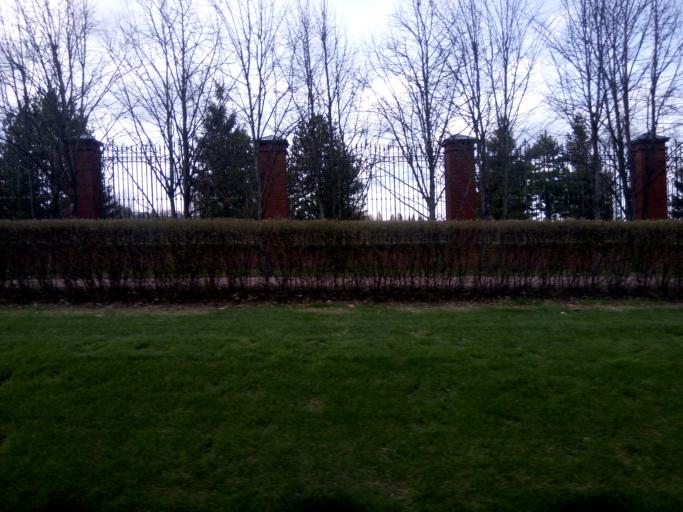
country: RU
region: Moskovskaya
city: Skolkovo
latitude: 55.6895
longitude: 37.3761
